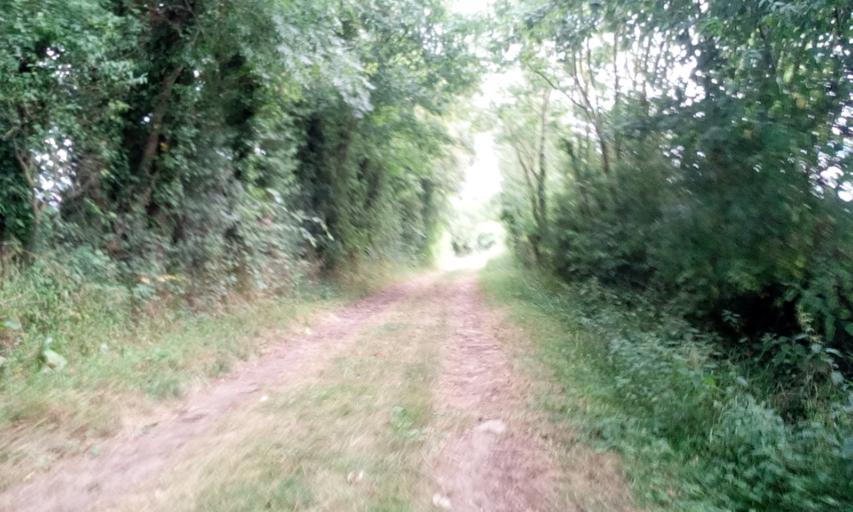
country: FR
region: Lower Normandy
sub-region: Departement du Calvados
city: Troarn
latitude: 49.1703
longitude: -0.1959
